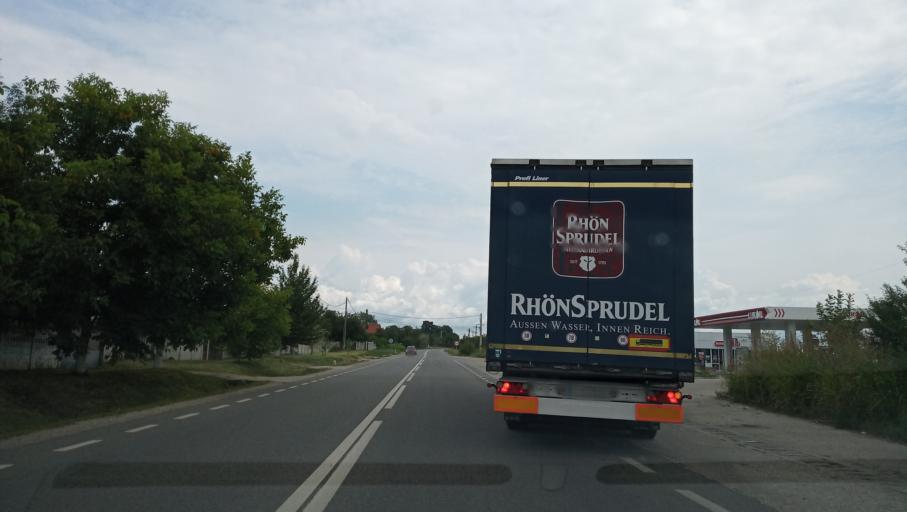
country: RO
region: Gorj
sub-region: Comuna Branesti
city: Branesti
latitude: 44.6813
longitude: 23.4226
